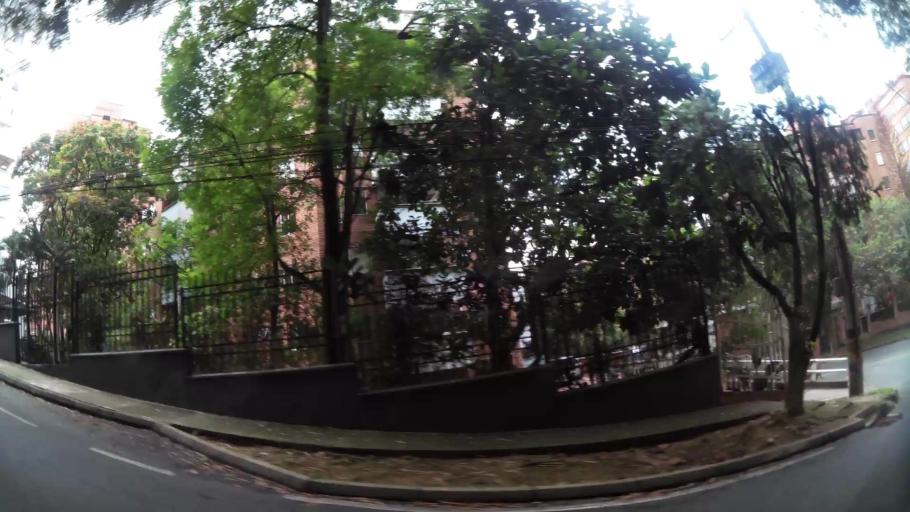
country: CO
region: Antioquia
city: Envigado
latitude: 6.1819
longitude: -75.5727
